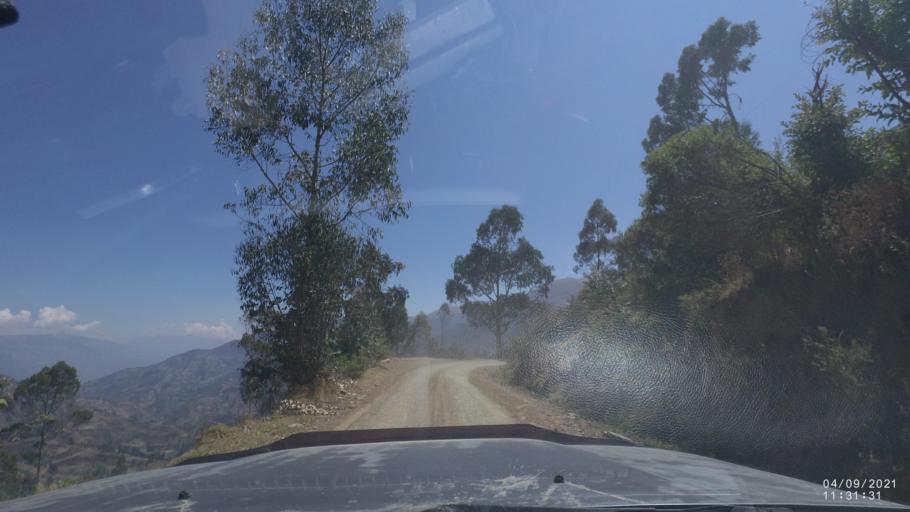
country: BO
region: Cochabamba
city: Colchani
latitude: -17.2325
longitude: -66.5213
